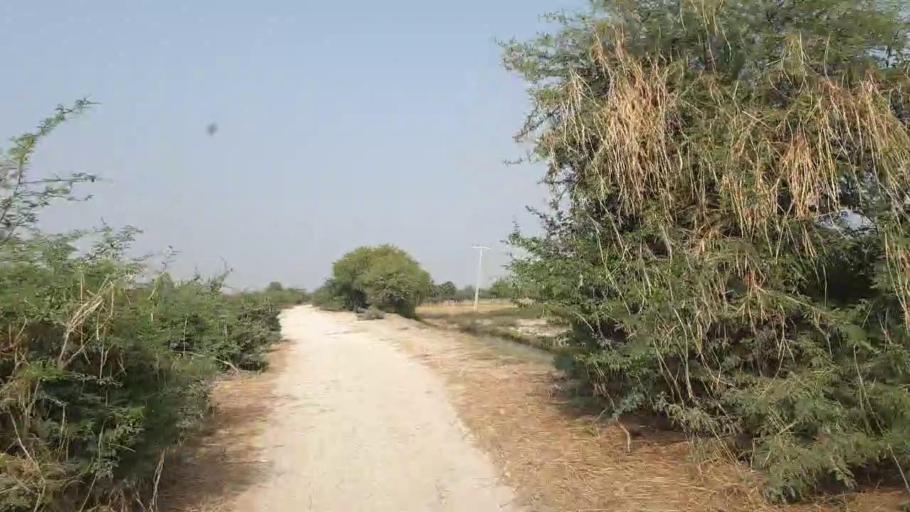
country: PK
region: Sindh
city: Kario
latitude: 24.9308
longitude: 68.6008
